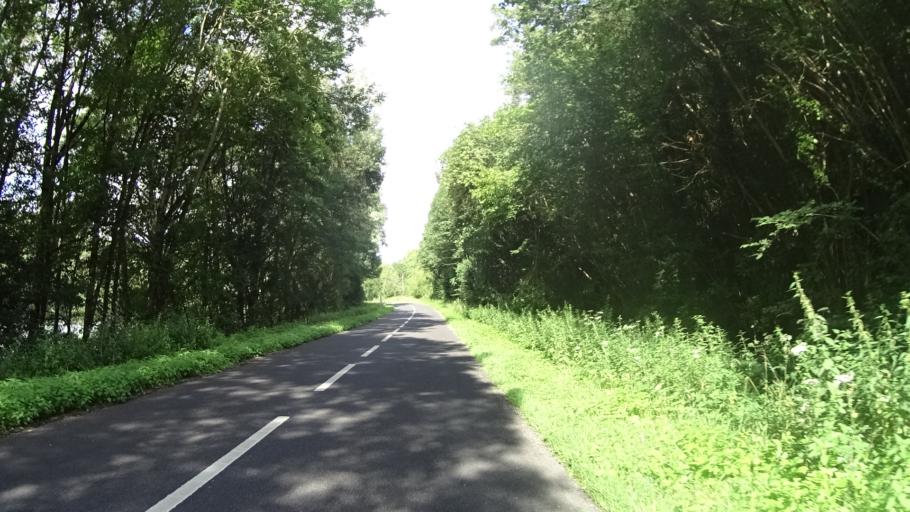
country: FR
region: Lorraine
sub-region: Departement de Meurthe-et-Moselle
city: Gondreville
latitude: 48.6458
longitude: 5.9647
